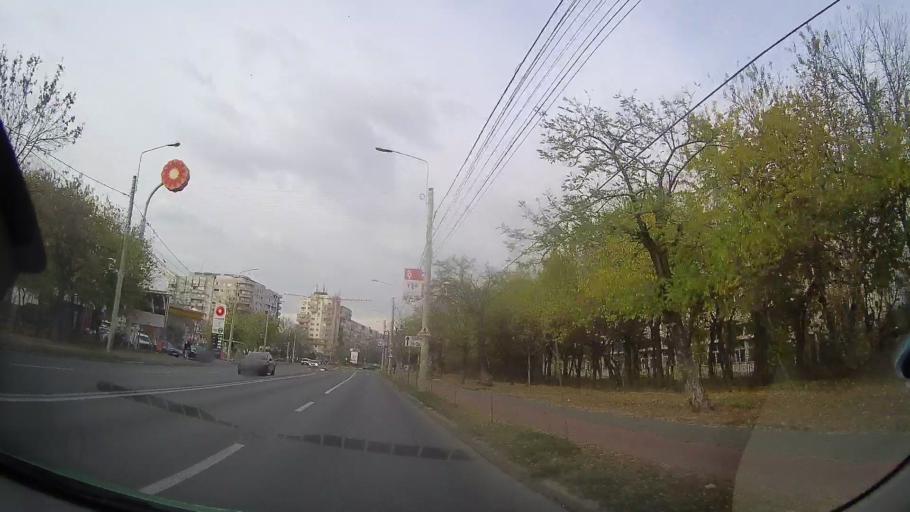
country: RO
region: Prahova
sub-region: Comuna Barcanesti
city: Tatarani
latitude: 44.9161
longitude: 26.0355
